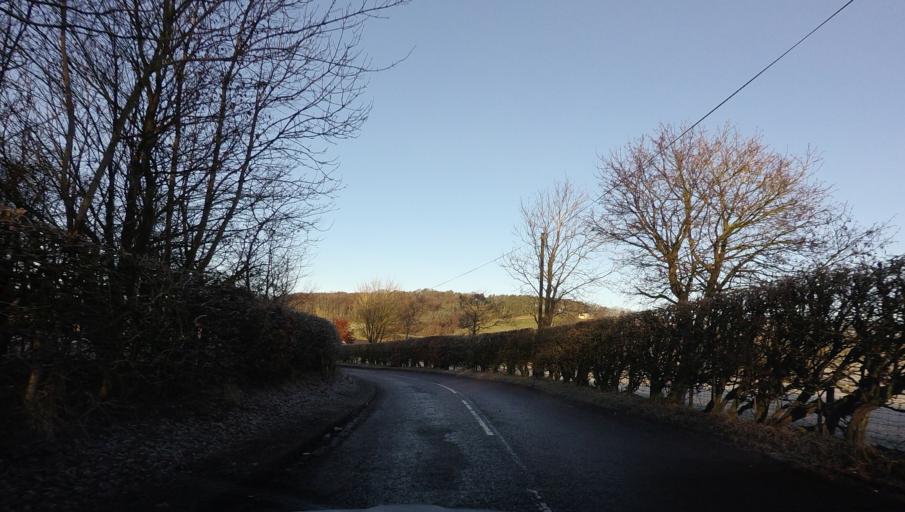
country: GB
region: Scotland
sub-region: North Lanarkshire
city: Shotts
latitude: 55.8294
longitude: -3.8213
